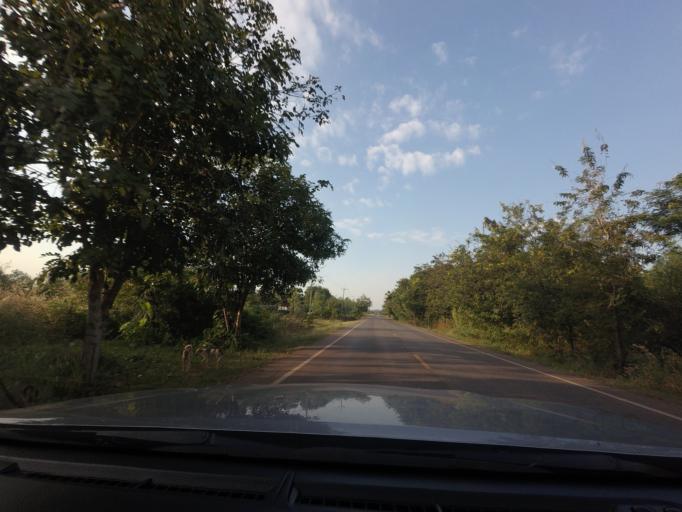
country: TH
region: Phitsanulok
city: Noen Maprang
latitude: 16.6051
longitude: 100.6213
